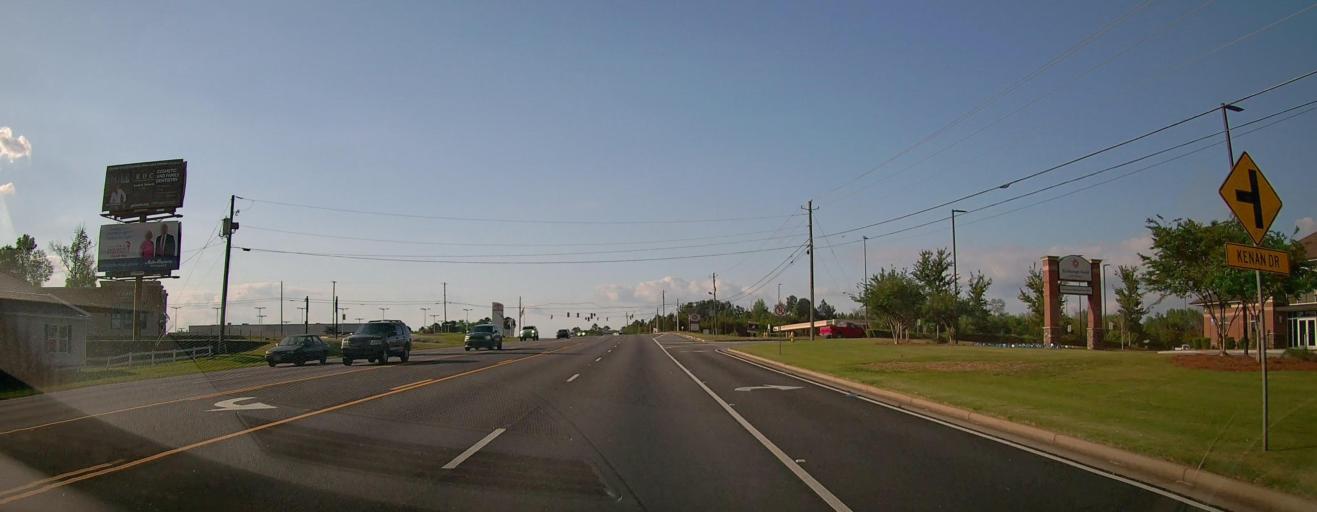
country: US
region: Georgia
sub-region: Baldwin County
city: Milledgeville
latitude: 33.1514
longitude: -83.2740
